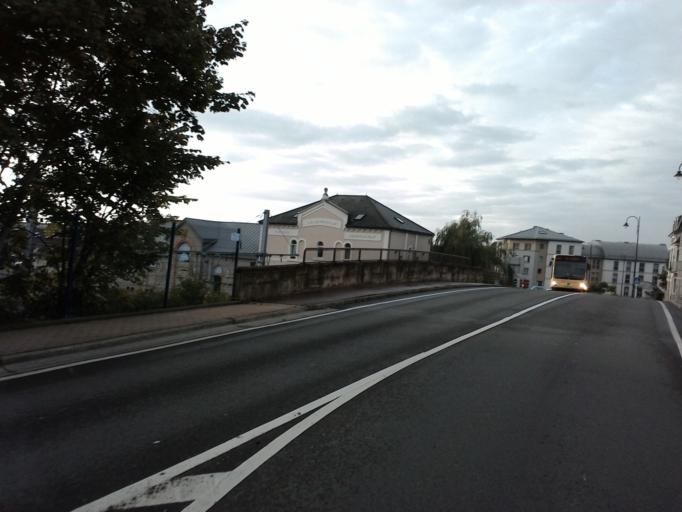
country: BE
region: Wallonia
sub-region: Province du Luxembourg
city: Arlon
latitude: 49.6814
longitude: 5.8057
